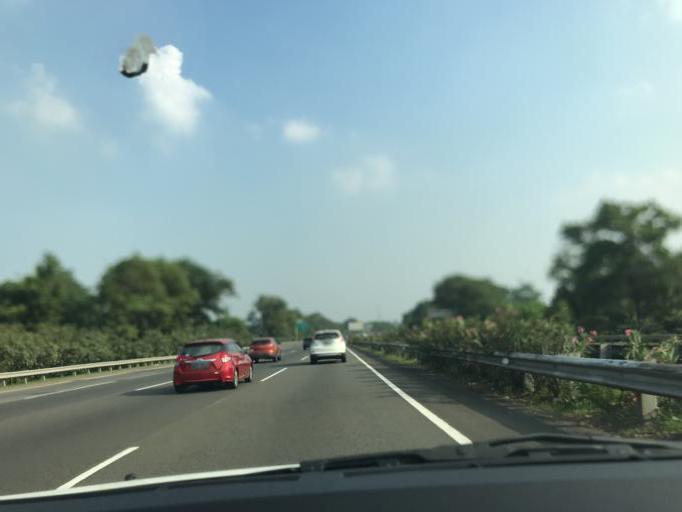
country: ID
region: West Java
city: Citeureup
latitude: -6.4436
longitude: 106.8926
